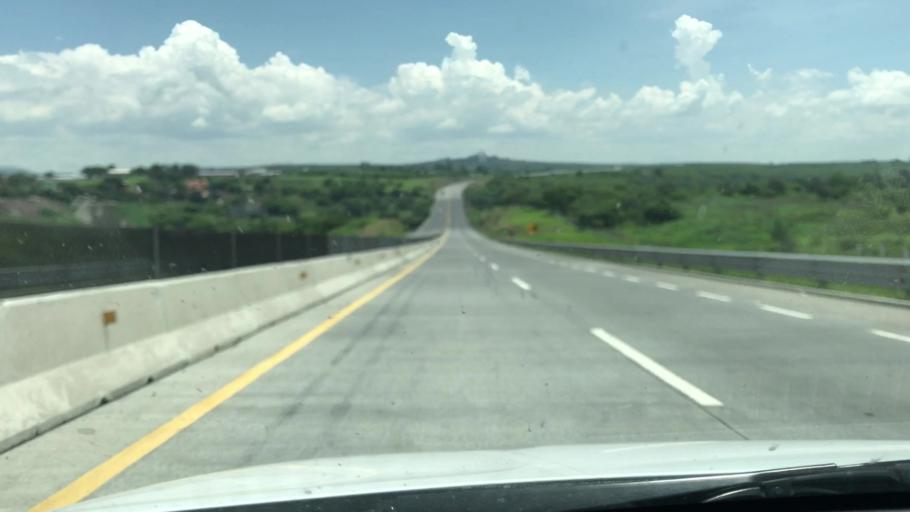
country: MX
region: Jalisco
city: Degollado
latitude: 20.3745
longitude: -102.1243
